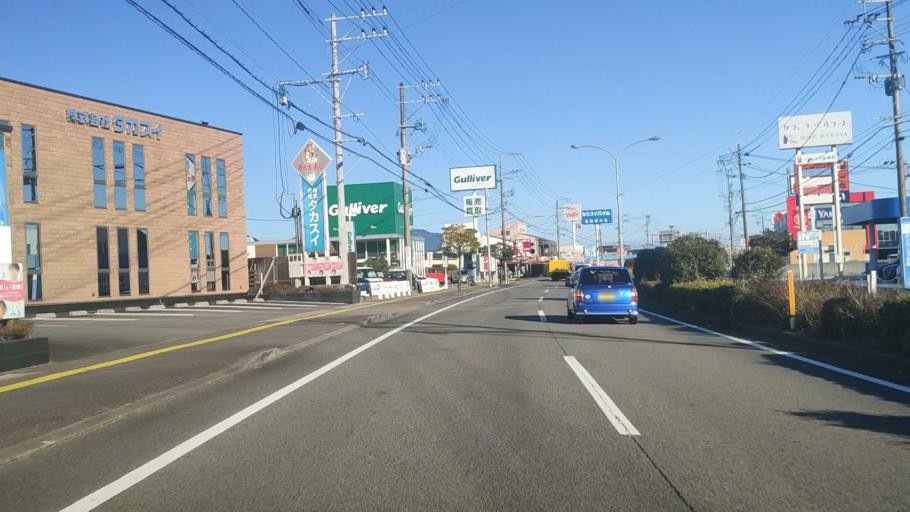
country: JP
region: Miyazaki
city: Nobeoka
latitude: 32.5485
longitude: 131.6770
